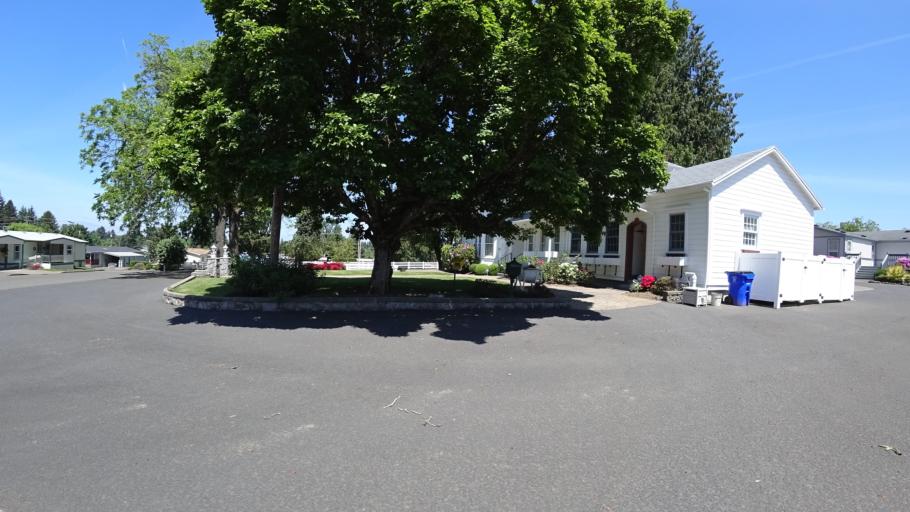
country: US
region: Oregon
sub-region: Clackamas County
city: Happy Valley
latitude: 45.4933
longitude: -122.4944
